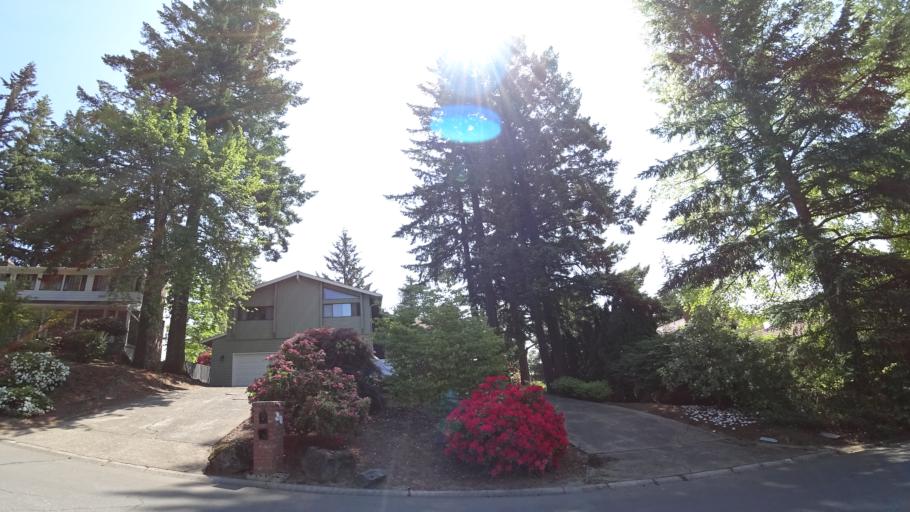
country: US
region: Oregon
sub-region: Clackamas County
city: Lake Oswego
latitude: 45.4248
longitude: -122.7135
